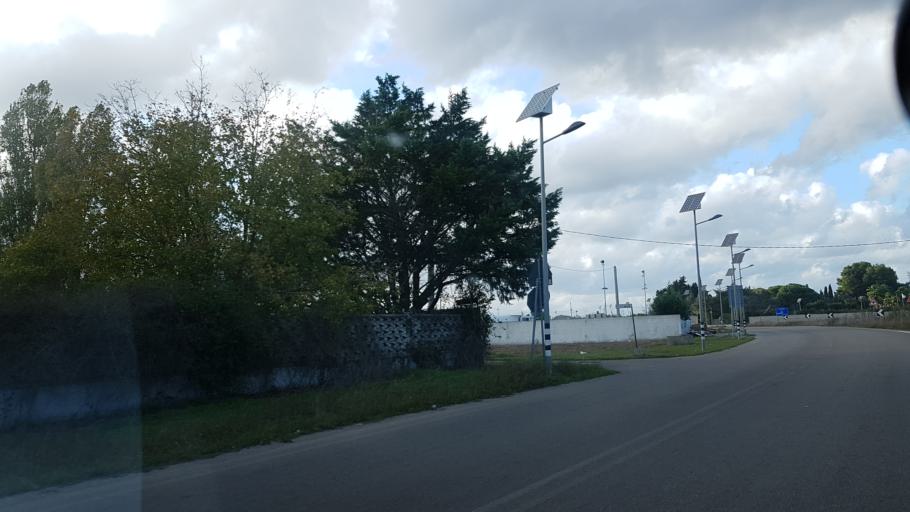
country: IT
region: Apulia
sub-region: Provincia di Brindisi
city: San Pietro Vernotico
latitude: 40.4977
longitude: 18.0061
